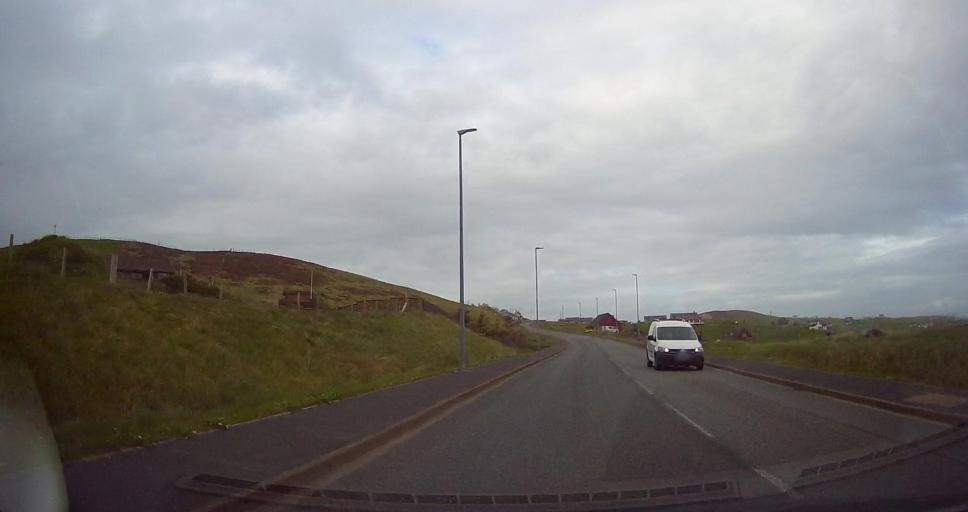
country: GB
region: Scotland
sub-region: Shetland Islands
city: Sandwick
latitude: 60.0408
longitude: -1.2299
